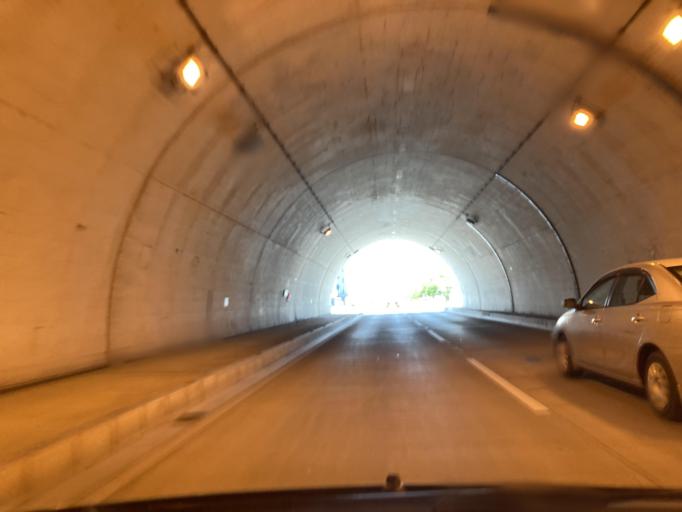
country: JP
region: Okinawa
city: Tomigusuku
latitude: 26.1885
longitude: 127.7183
